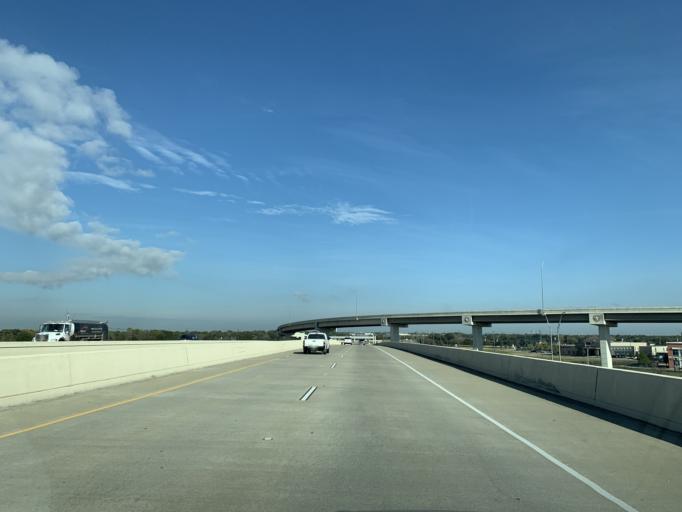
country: US
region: Texas
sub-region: Fort Bend County
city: Cinco Ranch
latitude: 29.7003
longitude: -95.7753
